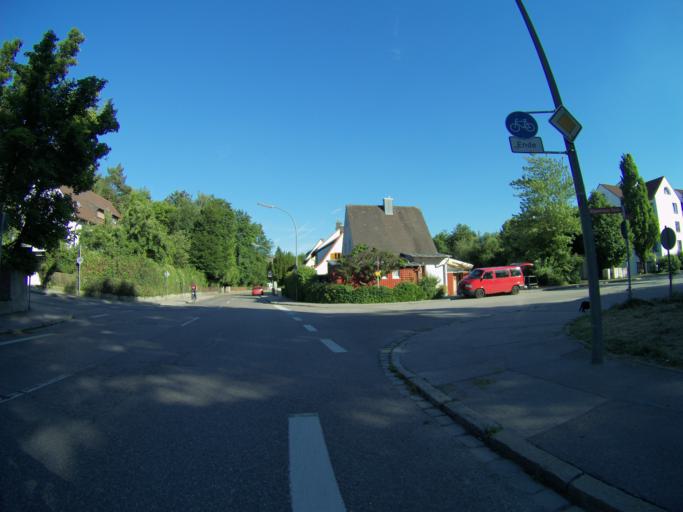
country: DE
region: Bavaria
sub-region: Upper Bavaria
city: Freising
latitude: 48.4046
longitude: 11.7333
